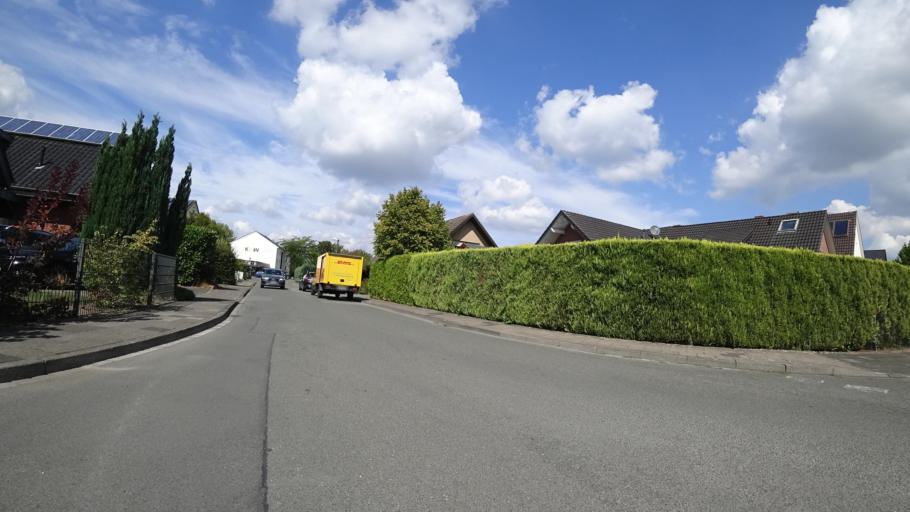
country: DE
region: North Rhine-Westphalia
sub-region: Regierungsbezirk Detmold
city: Guetersloh
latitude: 51.8750
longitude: 8.4335
